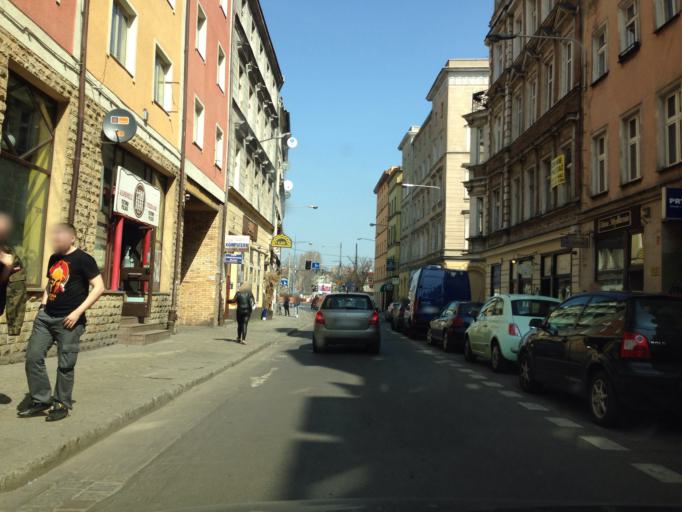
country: PL
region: Lower Silesian Voivodeship
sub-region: Powiat wroclawski
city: Wroclaw
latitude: 51.1125
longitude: 17.0314
